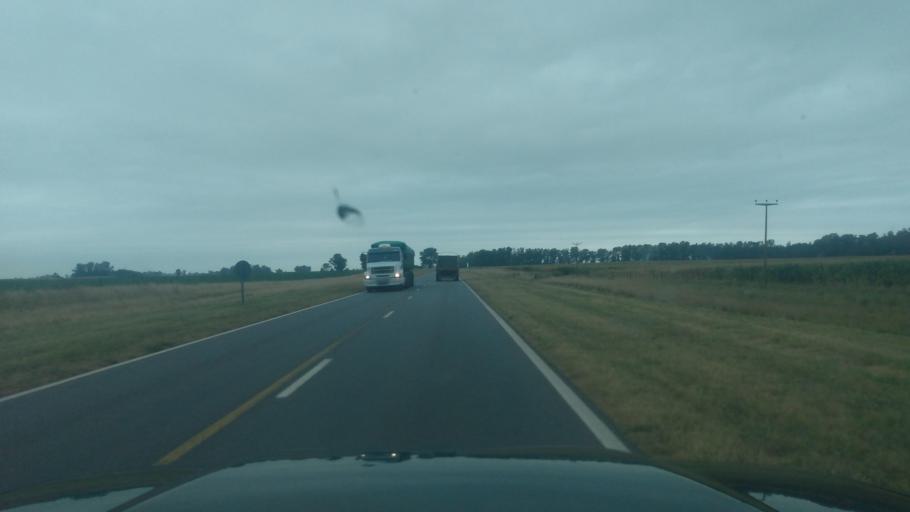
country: AR
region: Buenos Aires
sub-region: Partido de Nueve de Julio
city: Nueve de Julio
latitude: -35.4100
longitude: -60.7758
